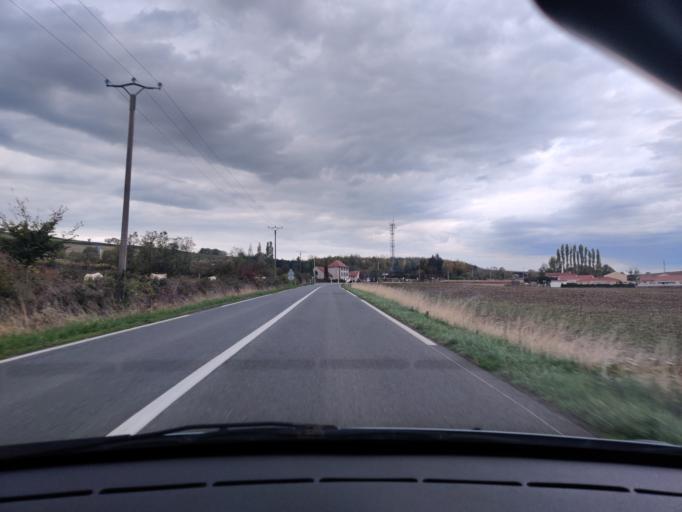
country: FR
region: Auvergne
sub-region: Departement du Puy-de-Dome
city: Combronde
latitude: 45.9668
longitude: 3.1038
